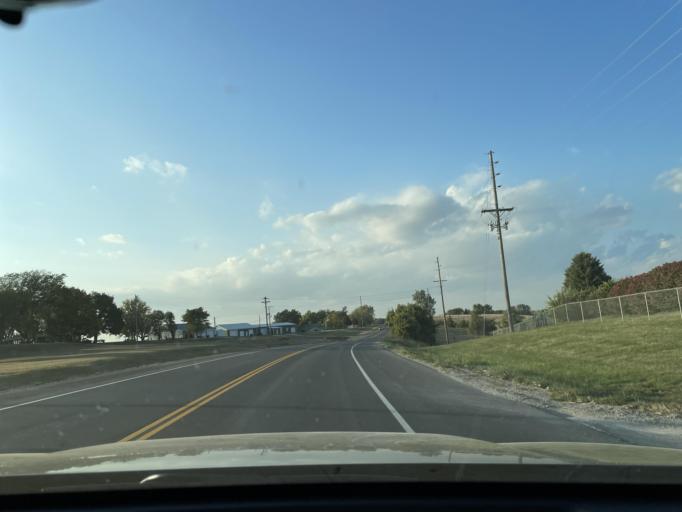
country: US
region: Missouri
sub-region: Andrew County
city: Country Club Village
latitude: 39.8297
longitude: -94.8601
